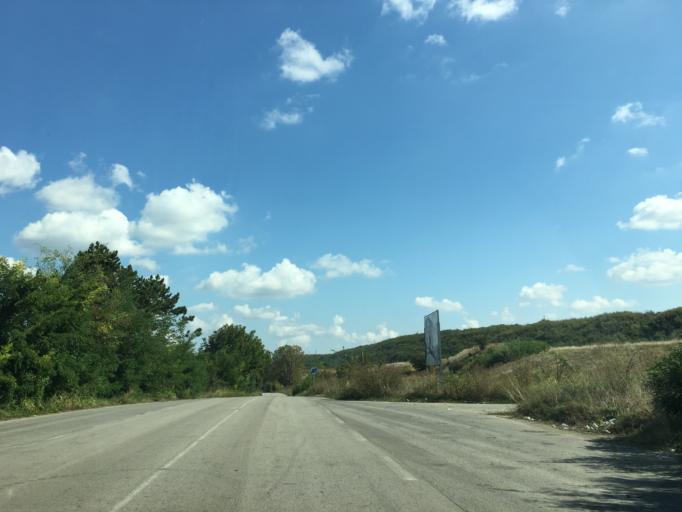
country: BG
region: Montana
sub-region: Obshtina Lom
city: Lom
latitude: 43.8079
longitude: 23.1688
